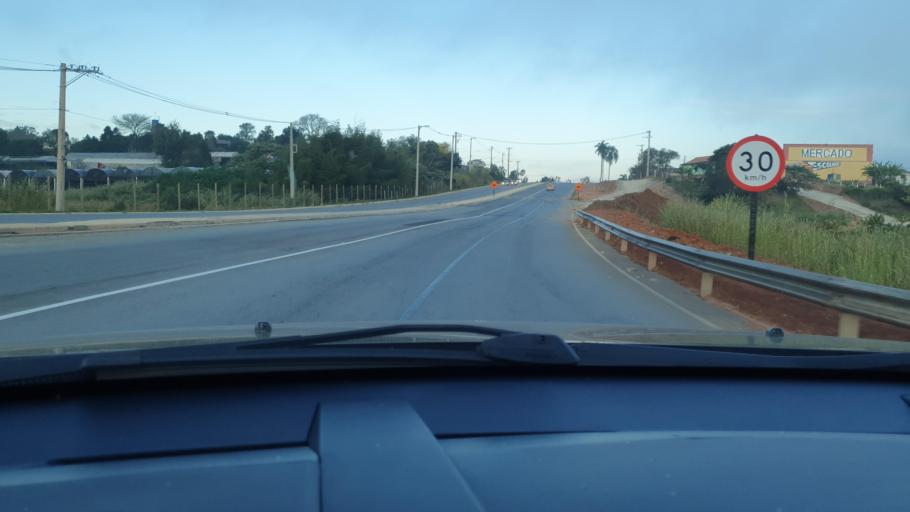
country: BR
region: Sao Paulo
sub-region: Vargem Grande Paulista
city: Vargem Grande Paulista
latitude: -23.6551
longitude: -47.0753
